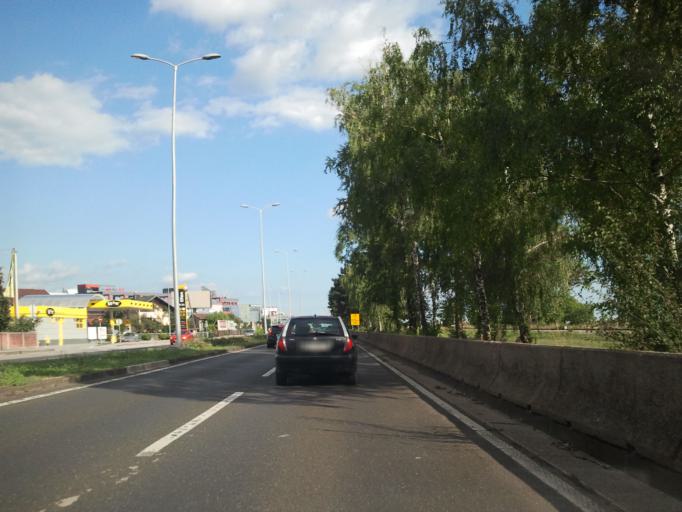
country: HR
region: Grad Zagreb
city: Odra
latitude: 45.7497
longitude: 15.9901
